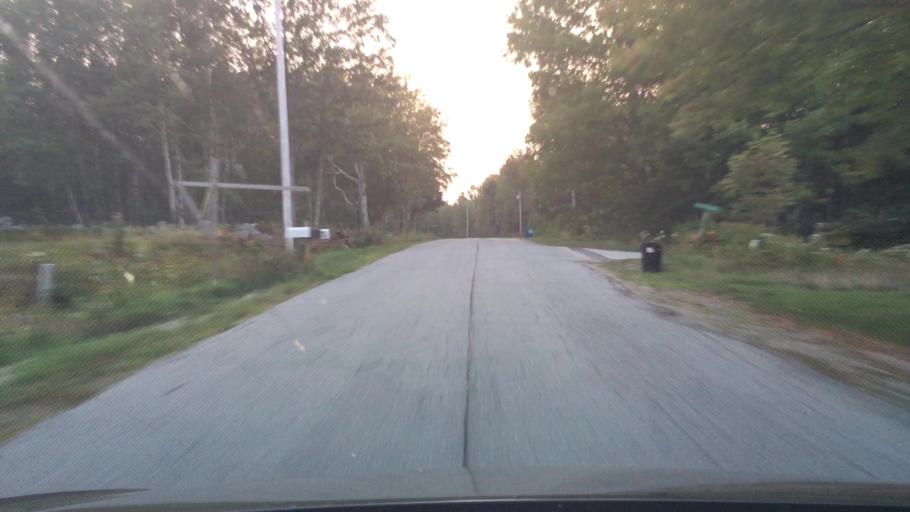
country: US
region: Maine
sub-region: Waldo County
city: Stockton Springs
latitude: 44.5293
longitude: -68.8654
